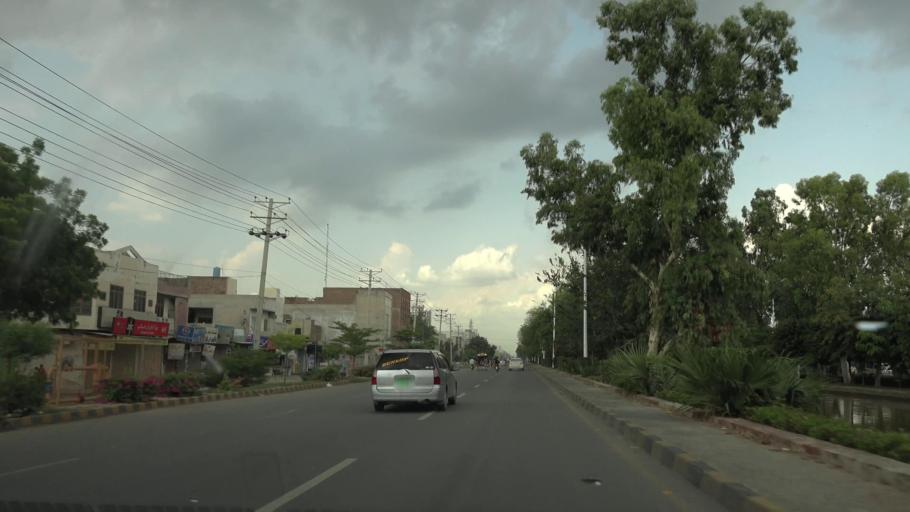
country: PK
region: Punjab
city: Faisalabad
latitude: 31.4356
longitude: 73.1273
